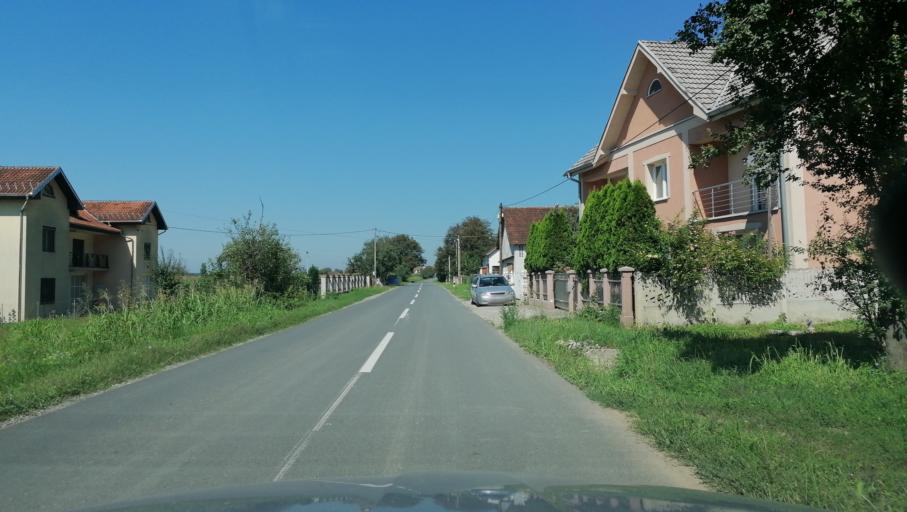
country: RS
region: Central Serbia
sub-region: Raski Okrug
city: Vrnjacka Banja
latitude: 43.6642
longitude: 20.9197
